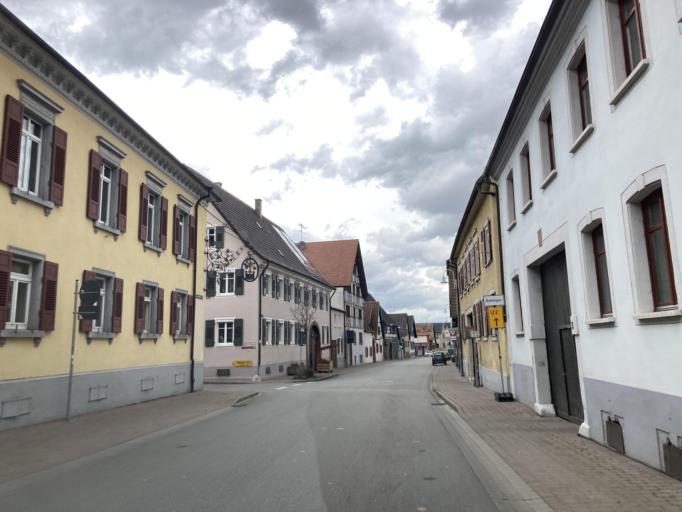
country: DE
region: Baden-Wuerttemberg
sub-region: Freiburg Region
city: Wyhl
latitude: 48.1330
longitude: 7.6562
